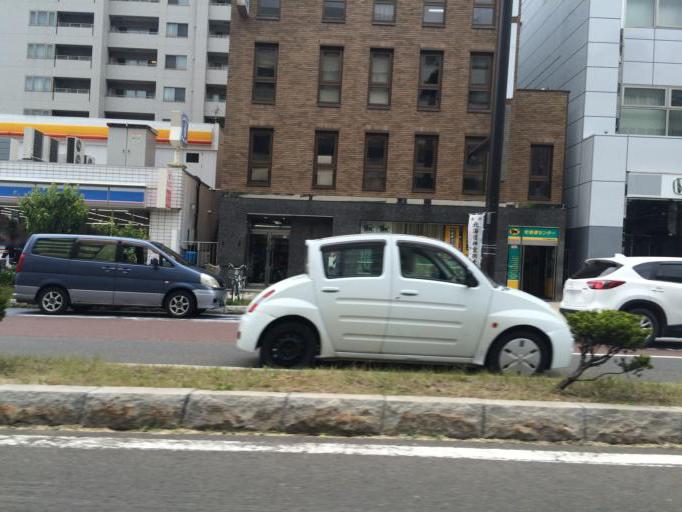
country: JP
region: Hokkaido
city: Sapporo
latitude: 43.0612
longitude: 141.3463
